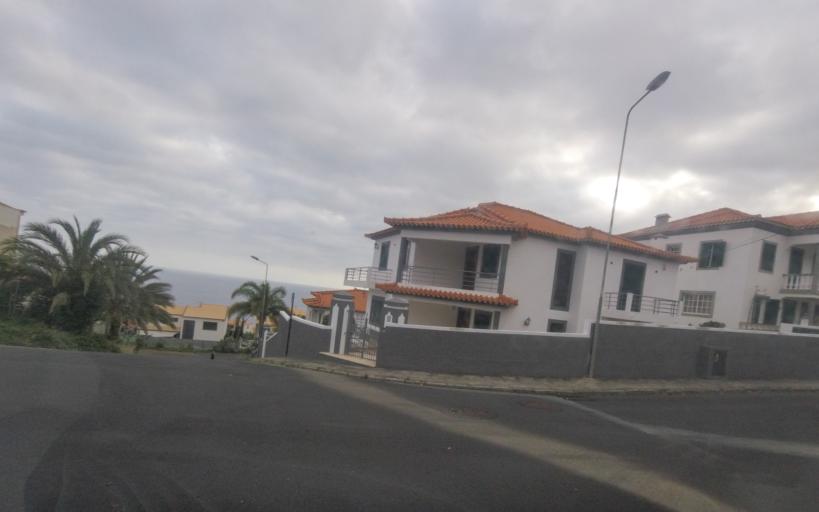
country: PT
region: Madeira
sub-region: Funchal
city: Nossa Senhora do Monte
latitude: 32.6535
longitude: -16.8924
